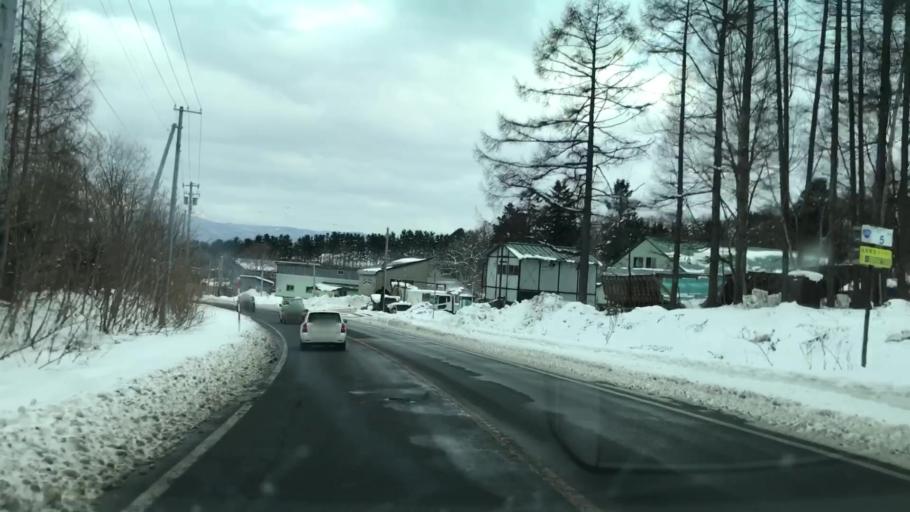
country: JP
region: Hokkaido
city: Yoichi
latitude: 43.2115
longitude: 140.7502
